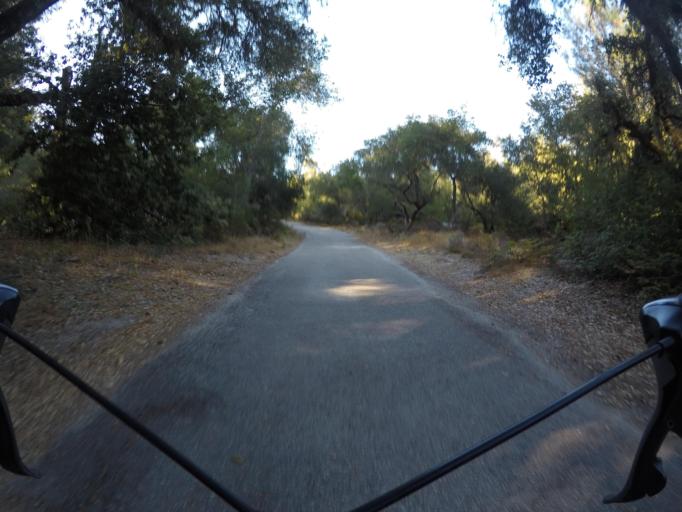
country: US
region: California
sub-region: Santa Cruz County
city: Brookdale
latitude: 37.1143
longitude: -122.1005
